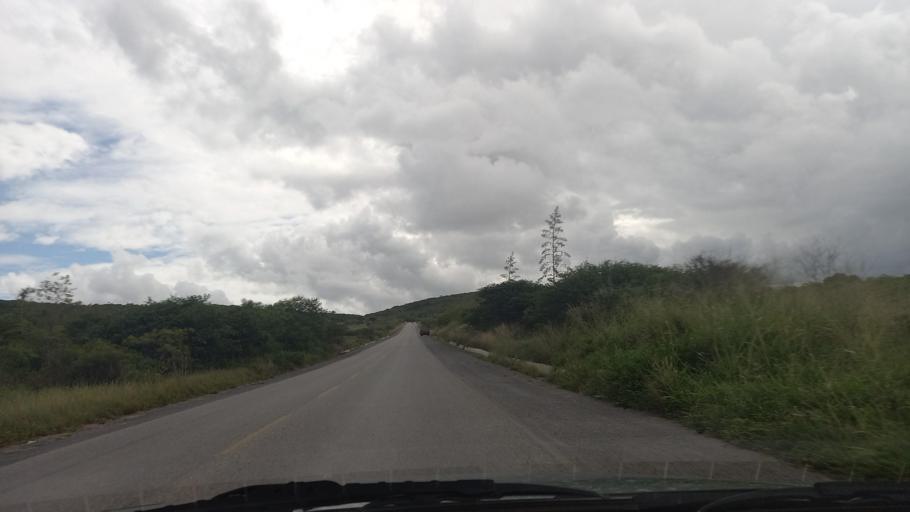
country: BR
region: Pernambuco
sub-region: Lajedo
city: Lajedo
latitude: -8.6721
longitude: -36.3911
